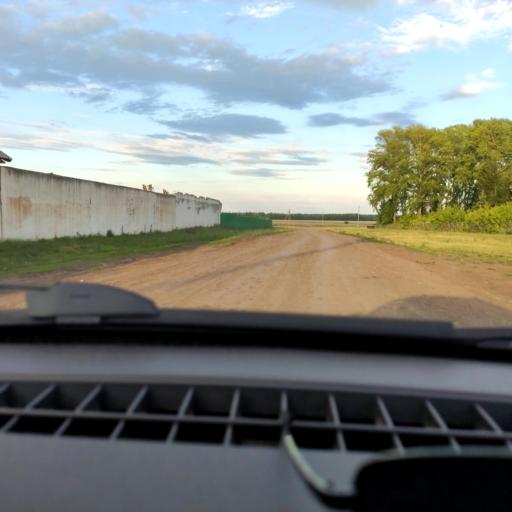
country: RU
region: Bashkortostan
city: Chishmy
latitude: 54.3773
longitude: 55.4218
